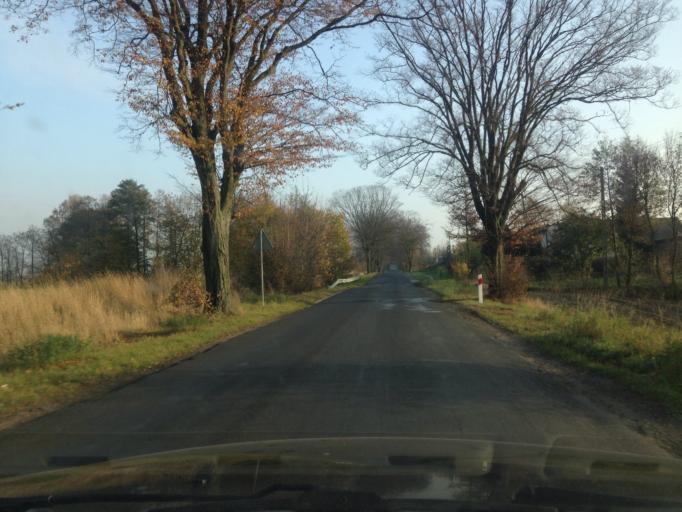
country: PL
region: Kujawsko-Pomorskie
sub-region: Powiat wabrzeski
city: Debowa Laka
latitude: 53.2499
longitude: 19.1229
